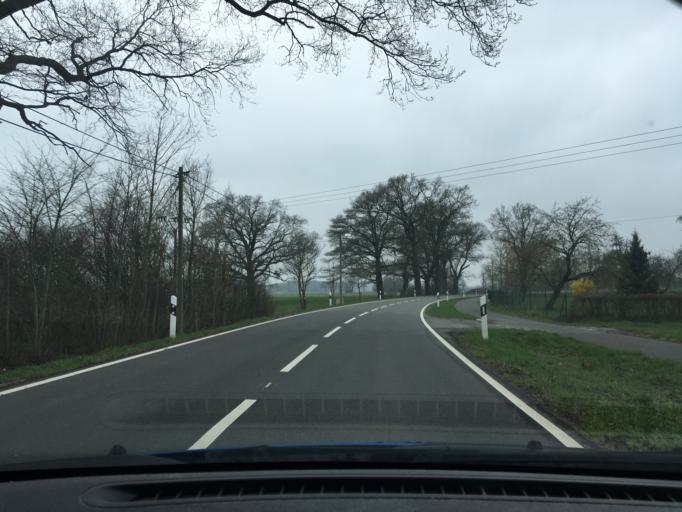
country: DE
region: Lower Saxony
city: Neu Darchau
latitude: 53.2908
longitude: 10.8871
